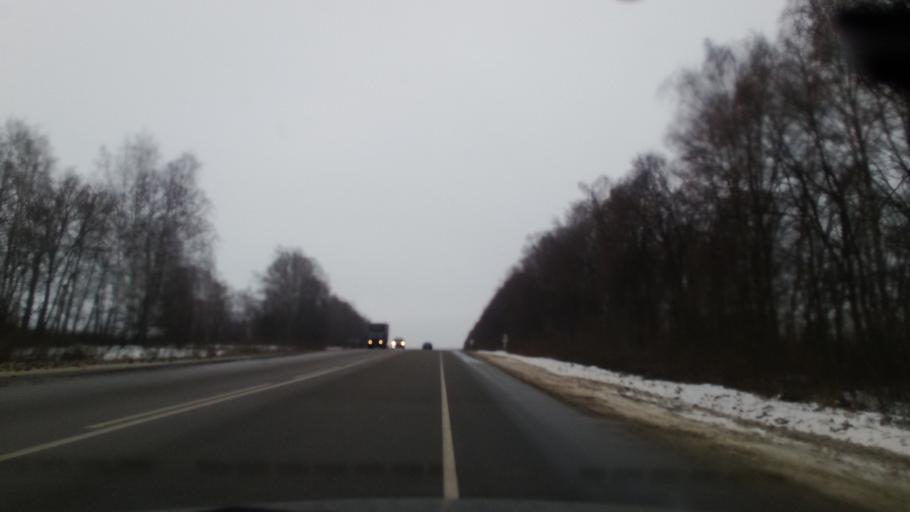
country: RU
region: Tula
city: Bolokhovo
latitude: 54.0421
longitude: 37.8626
